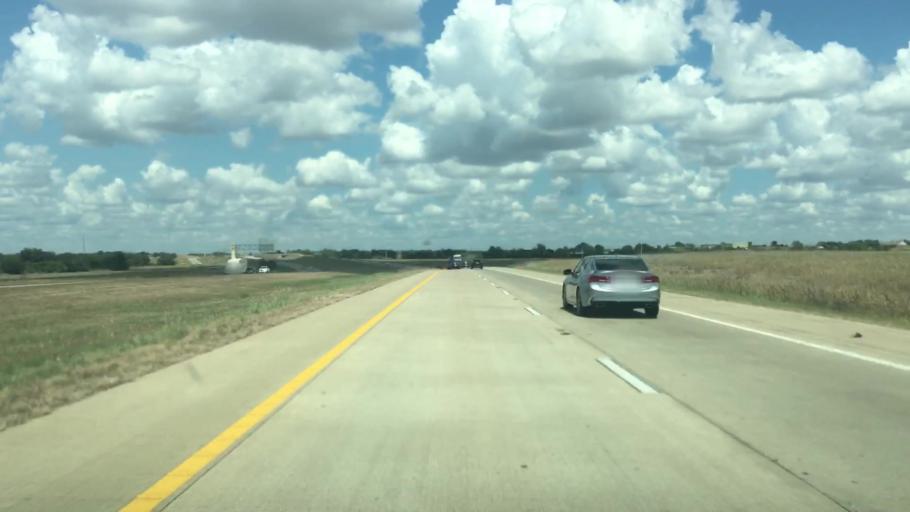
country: US
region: Texas
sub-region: Williamson County
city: Hutto
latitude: 30.5530
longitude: -97.5765
